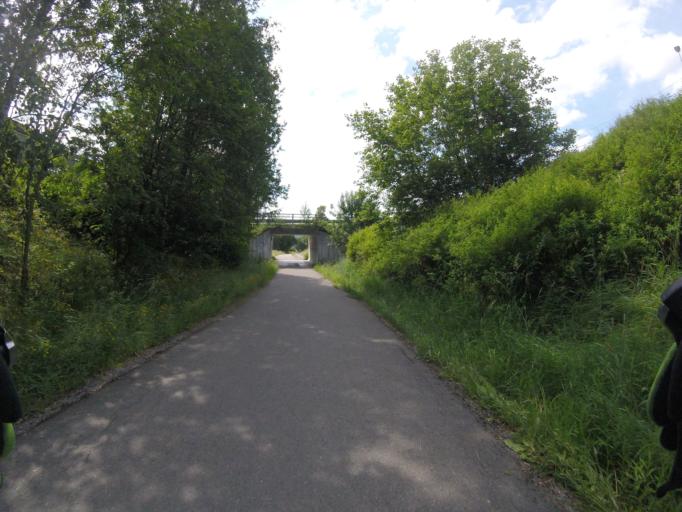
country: NO
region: Akershus
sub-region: Skedsmo
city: Lillestrom
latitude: 59.9730
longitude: 11.0554
